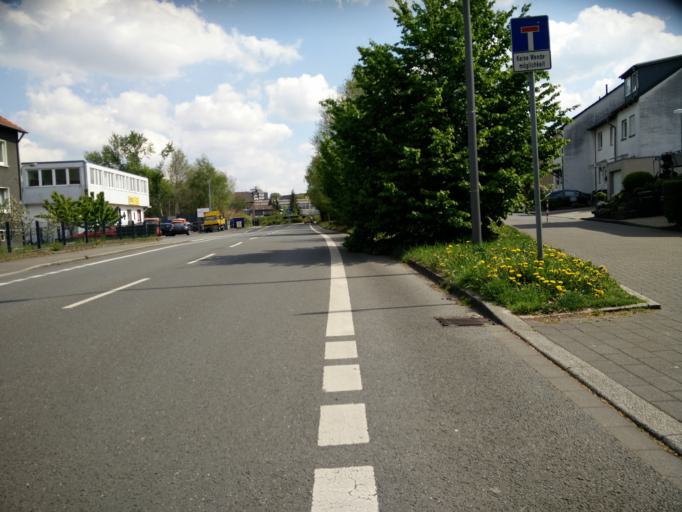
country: DE
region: North Rhine-Westphalia
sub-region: Regierungsbezirk Arnsberg
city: Bochum
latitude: 51.5116
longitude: 7.2060
